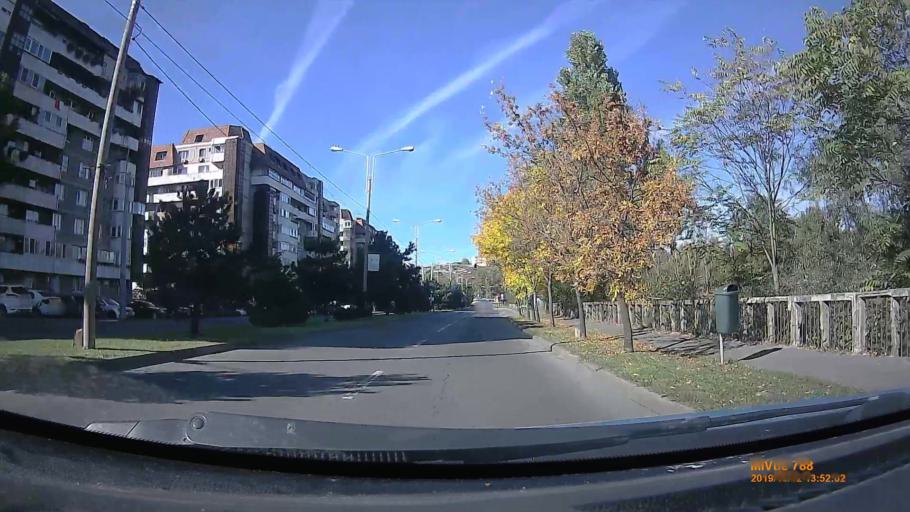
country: RO
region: Bihor
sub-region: Comuna Biharea
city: Oradea
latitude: 47.0483
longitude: 21.9624
